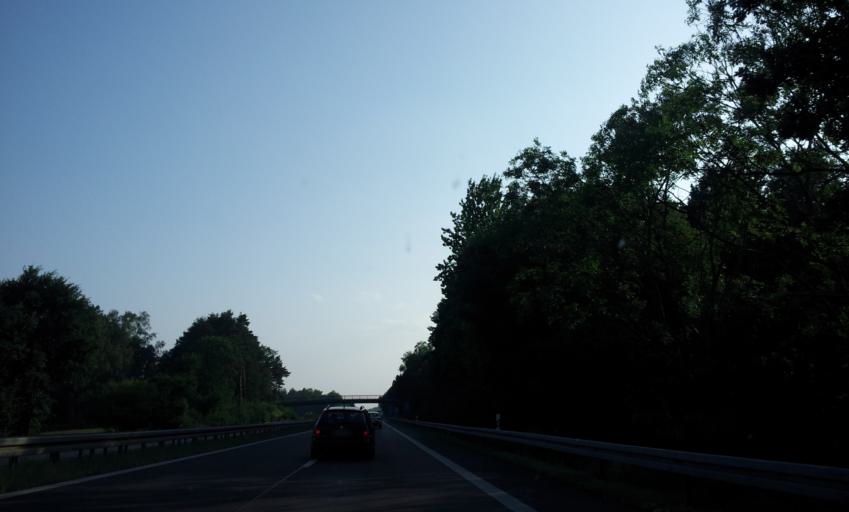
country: DE
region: Brandenburg
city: Britz
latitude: 52.8991
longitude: 13.7305
